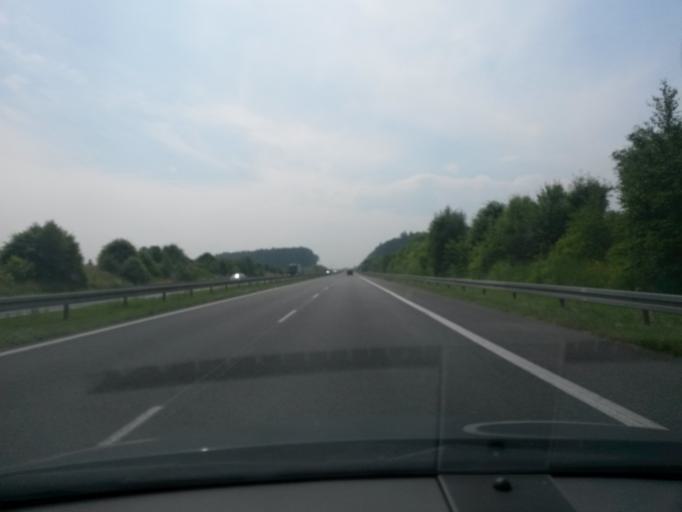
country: PL
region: Lodz Voivodeship
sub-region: Powiat piotrkowski
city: Wola Krzysztoporska
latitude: 51.3072
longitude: 19.5623
